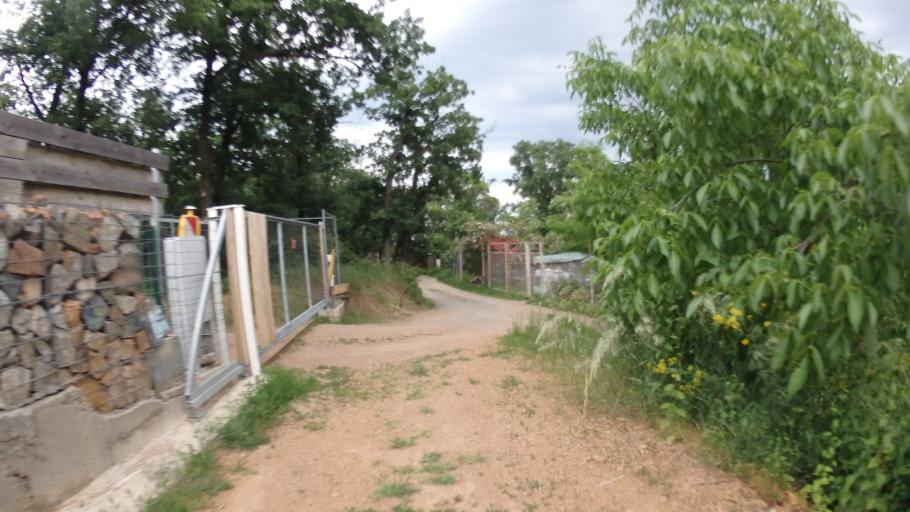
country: CZ
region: South Moravian
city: Ostopovice
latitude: 49.1342
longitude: 16.5442
